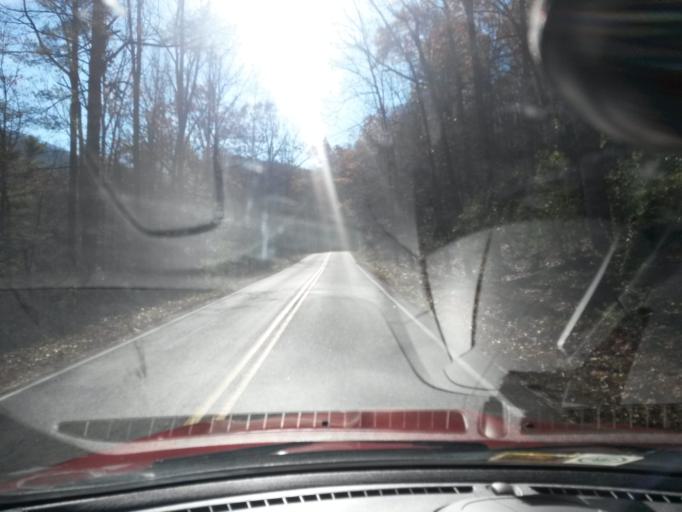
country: US
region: Virginia
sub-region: Botetourt County
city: Buchanan
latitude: 37.5133
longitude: -79.6666
